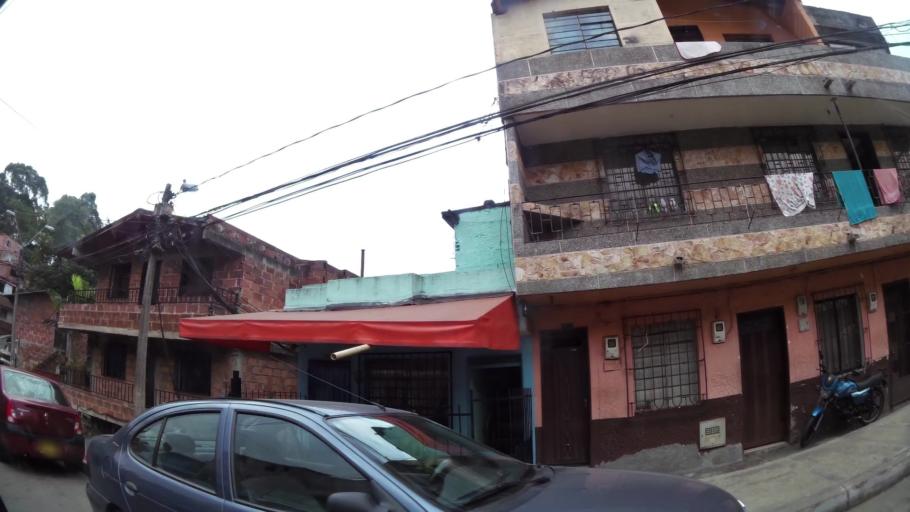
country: CO
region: Antioquia
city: Medellin
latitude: 6.2818
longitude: -75.5484
